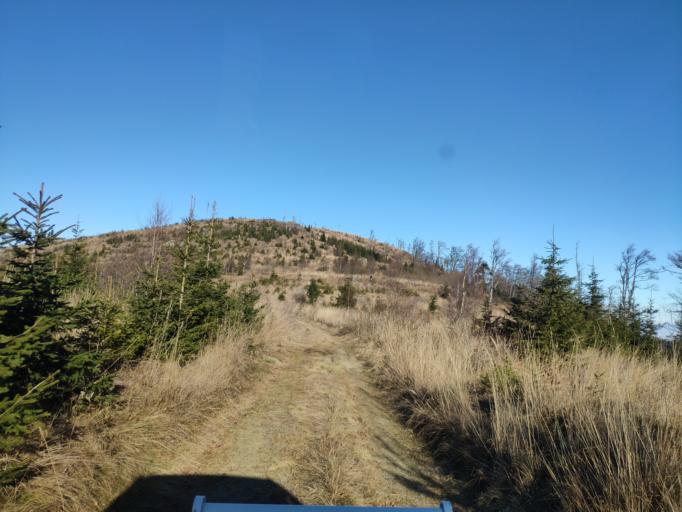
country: SK
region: Kosicky
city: Dobsina
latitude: 48.8250
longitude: 20.4637
